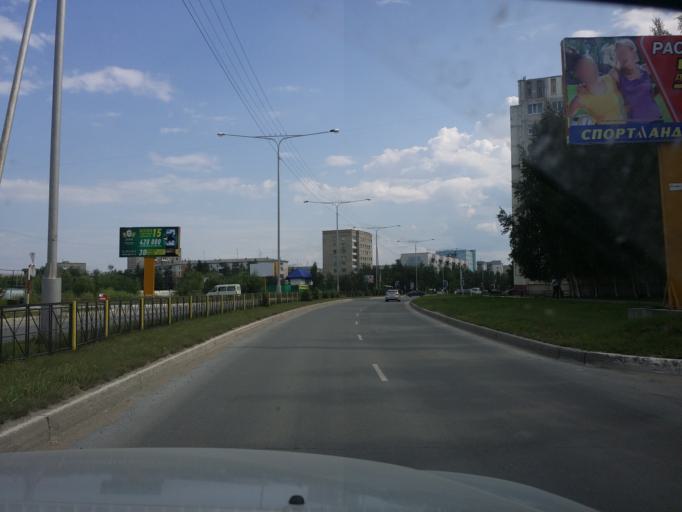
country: RU
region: Khanty-Mansiyskiy Avtonomnyy Okrug
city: Nizhnevartovsk
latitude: 60.9475
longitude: 76.5653
